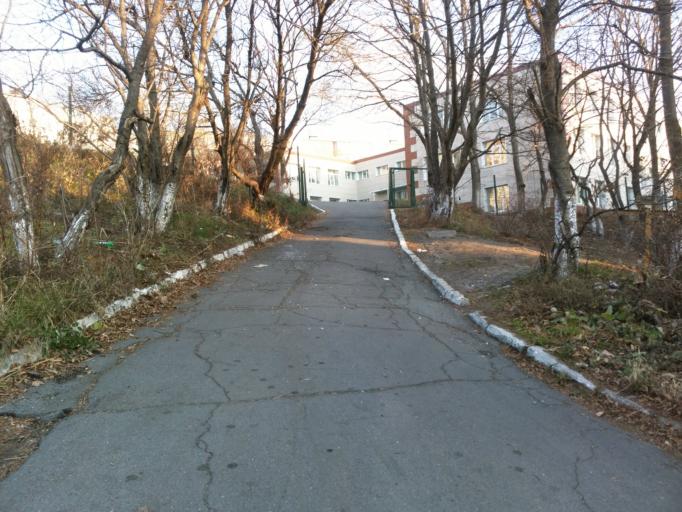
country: RU
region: Primorskiy
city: Vladivostok
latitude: 43.0895
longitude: 131.9726
